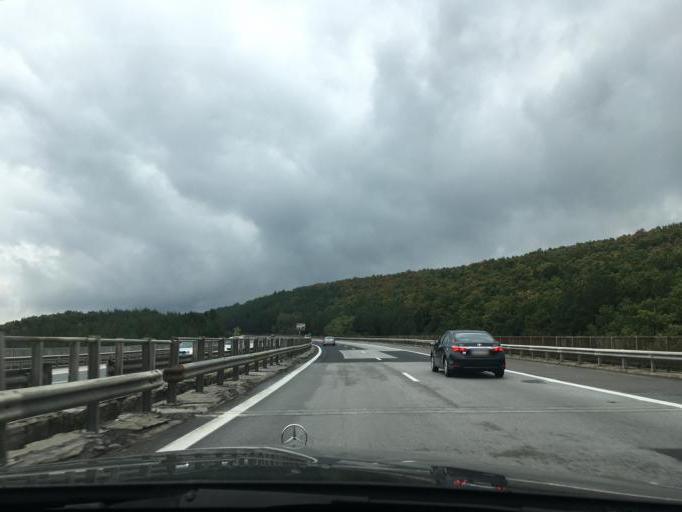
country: BG
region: Sofiya
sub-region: Obshtina Elin Pelin
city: Elin Pelin
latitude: 42.5911
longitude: 23.6230
